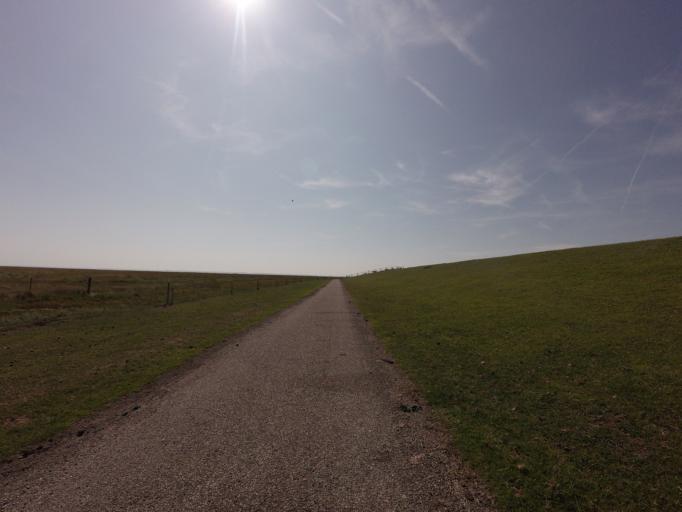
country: NL
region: Friesland
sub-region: Gemeente Schiermonnikoog
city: Schiermonnikoog
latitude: 53.4775
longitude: 6.2102
